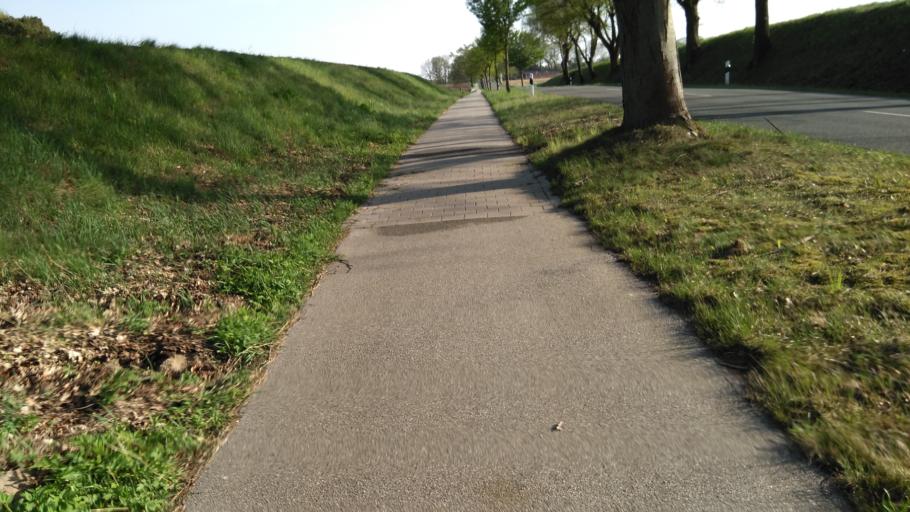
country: DE
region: Lower Saxony
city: Apensen
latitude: 53.4353
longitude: 9.6571
